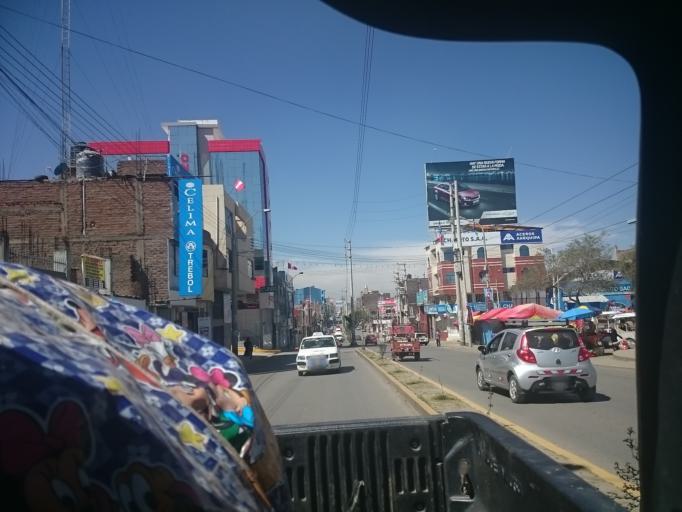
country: PE
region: Junin
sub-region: Provincia de Huancayo
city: El Tambo
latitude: -12.0485
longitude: -75.2228
